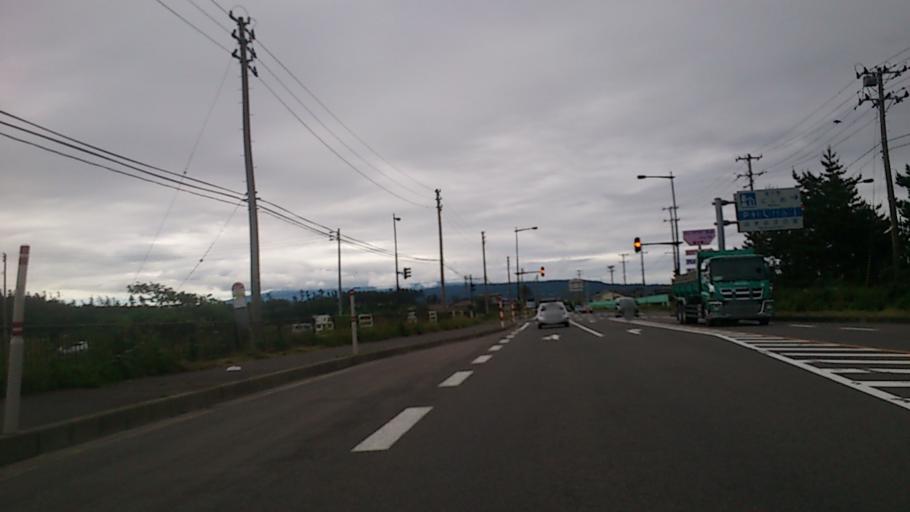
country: JP
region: Yamagata
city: Yuza
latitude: 39.3629
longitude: 140.0160
